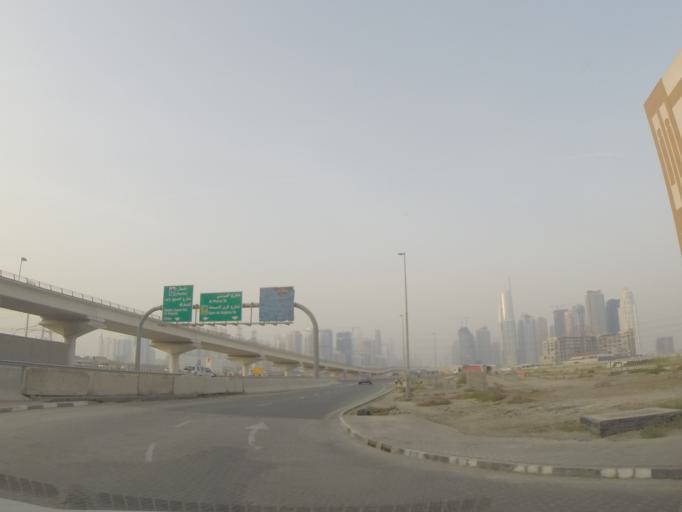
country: AE
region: Dubai
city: Dubai
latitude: 25.0579
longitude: 55.1278
